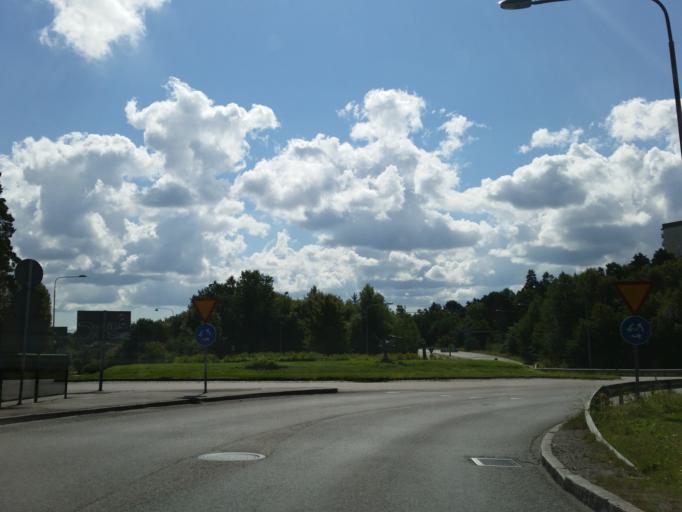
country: SE
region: Stockholm
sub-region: Solna Kommun
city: Solna
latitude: 59.3502
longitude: 18.0057
